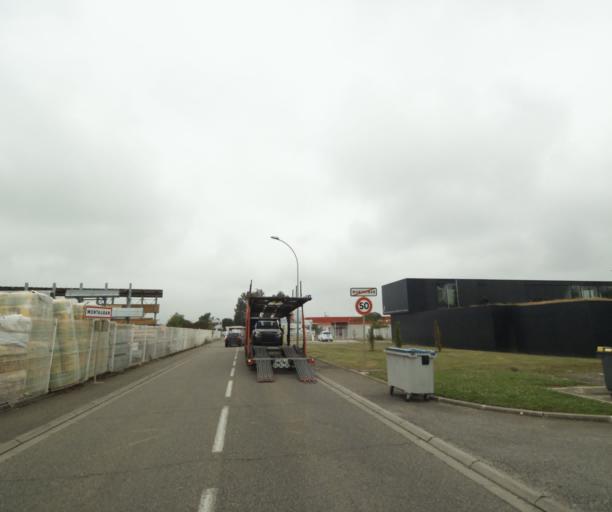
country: FR
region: Midi-Pyrenees
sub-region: Departement du Tarn-et-Garonne
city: Montauban
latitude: 43.9969
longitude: 1.3369
